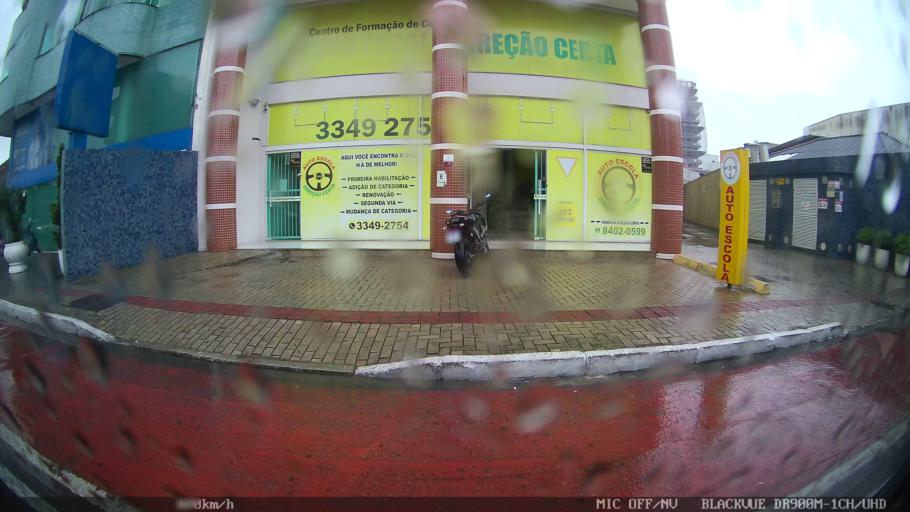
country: BR
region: Santa Catarina
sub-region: Itajai
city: Itajai
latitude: -26.9054
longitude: -48.6686
